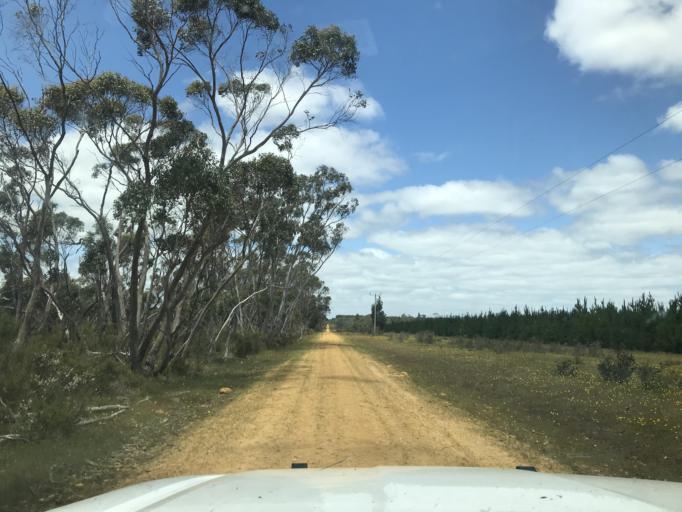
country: AU
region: South Australia
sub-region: Wattle Range
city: Penola
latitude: -37.3657
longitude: 141.1557
